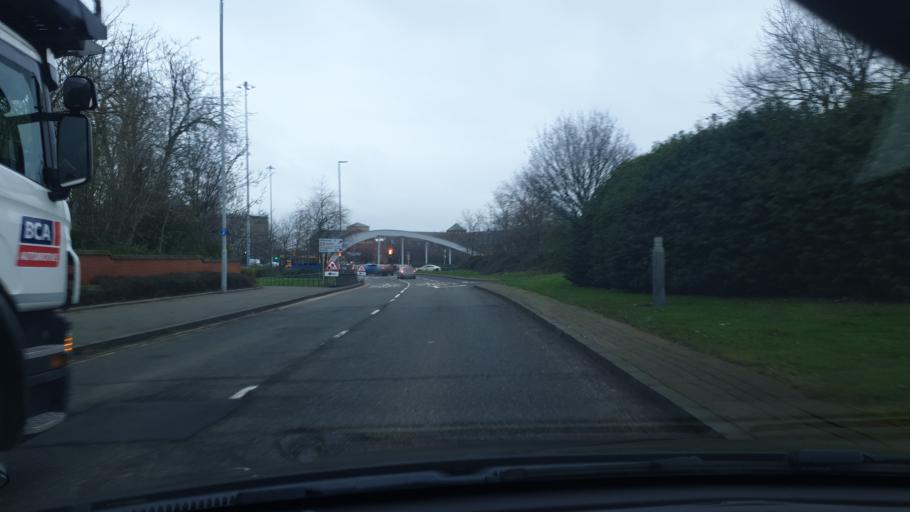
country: GB
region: England
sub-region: Wolverhampton
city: Wolverhampton
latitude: 52.5823
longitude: -2.1225
